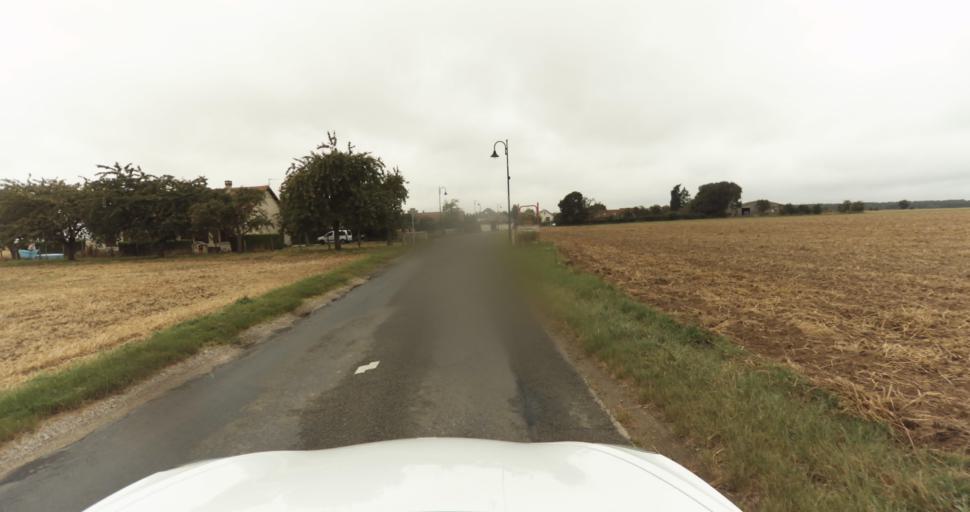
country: FR
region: Haute-Normandie
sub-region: Departement de l'Eure
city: Aviron
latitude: 49.0724
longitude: 1.0934
